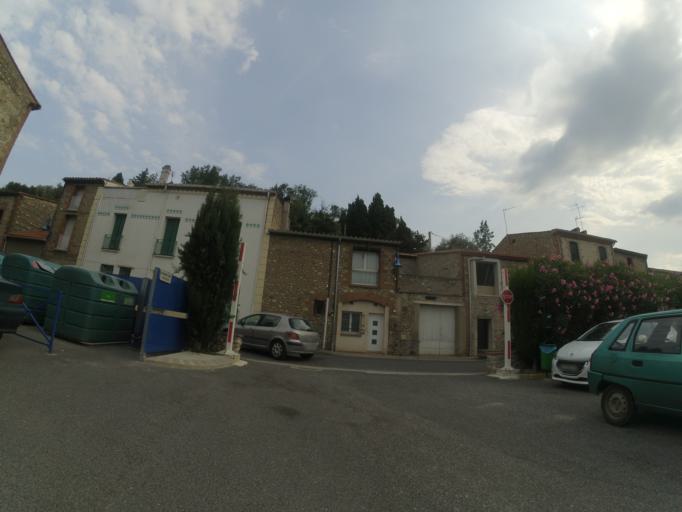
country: FR
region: Languedoc-Roussillon
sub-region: Departement des Pyrenees-Orientales
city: Corneilla-la-Riviere
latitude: 42.6818
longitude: 2.7405
